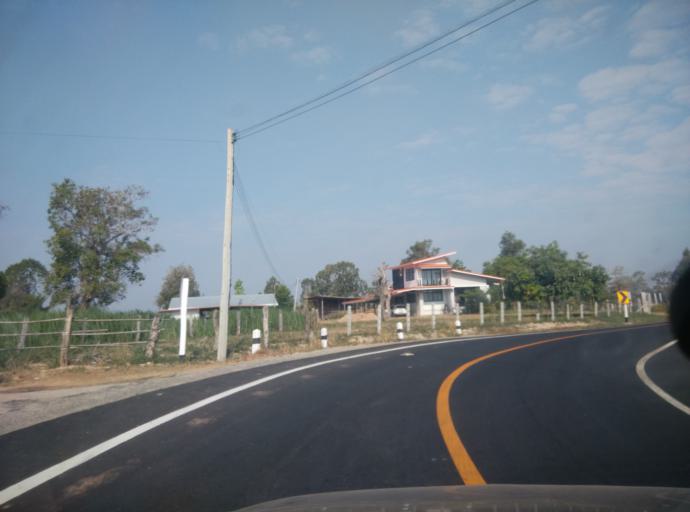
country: TH
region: Sisaket
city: Si Sa Ket
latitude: 15.1194
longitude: 104.2515
